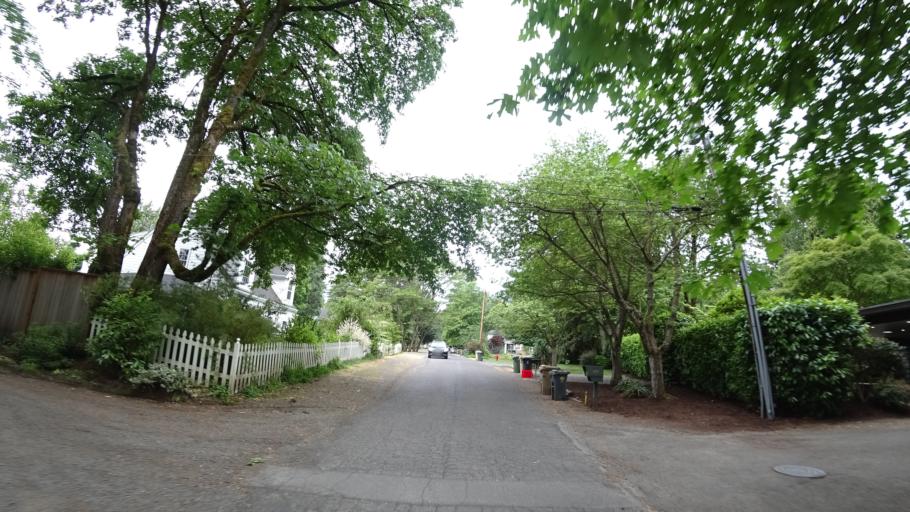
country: US
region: Oregon
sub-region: Clackamas County
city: Lake Oswego
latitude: 45.4264
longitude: -122.6697
